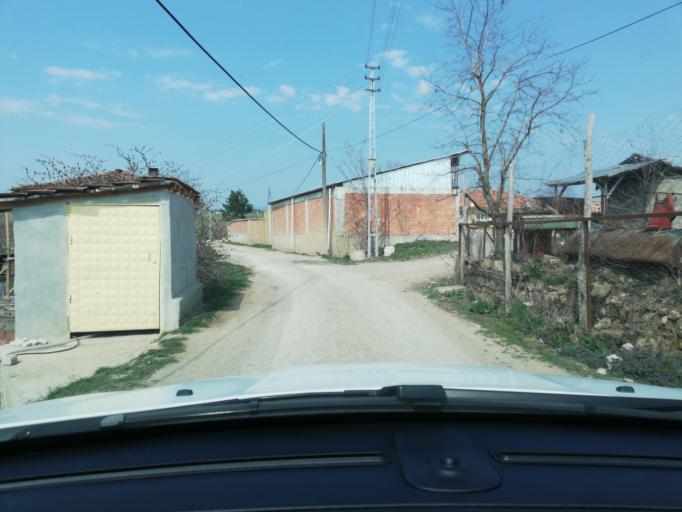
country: TR
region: Kastamonu
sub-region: Cide
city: Kastamonu
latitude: 41.4594
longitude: 33.7575
